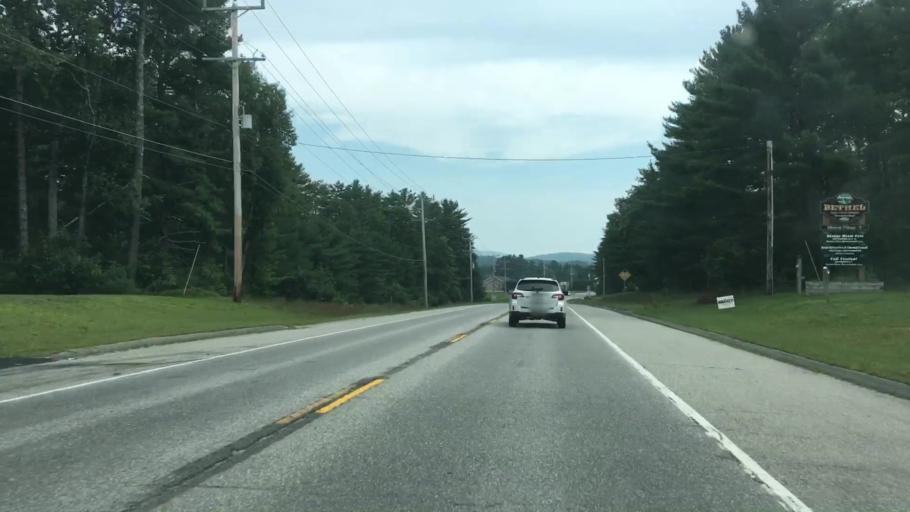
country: US
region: Maine
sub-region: Oxford County
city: Bethel
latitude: 44.4288
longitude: -70.7992
